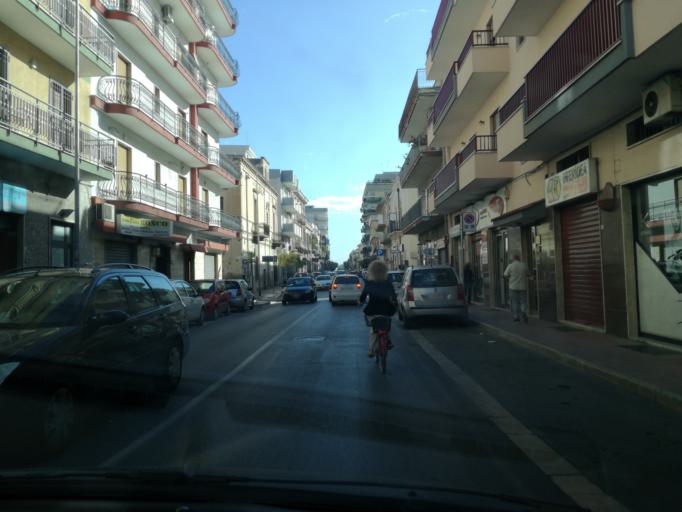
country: IT
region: Apulia
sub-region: Provincia di Bari
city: Triggiano
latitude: 41.0654
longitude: 16.9213
